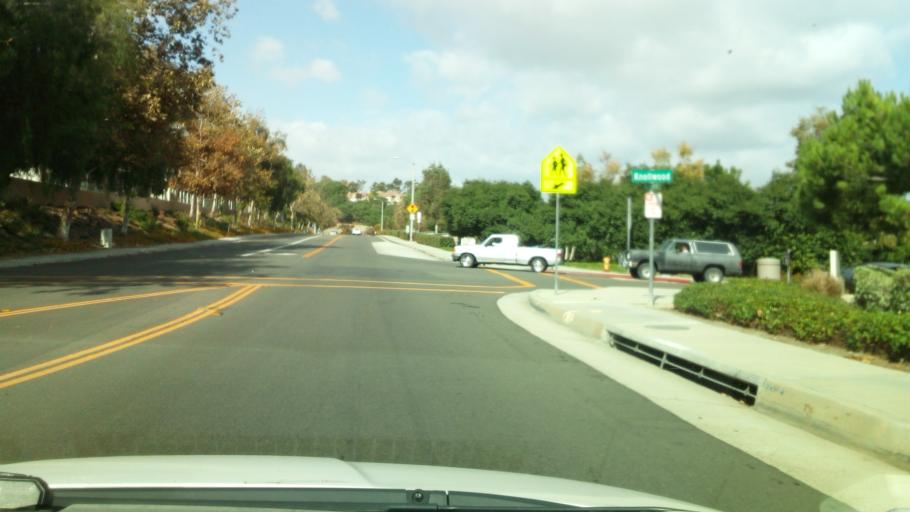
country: US
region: California
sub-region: Orange County
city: Aliso Viejo
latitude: 33.5534
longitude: -117.7222
